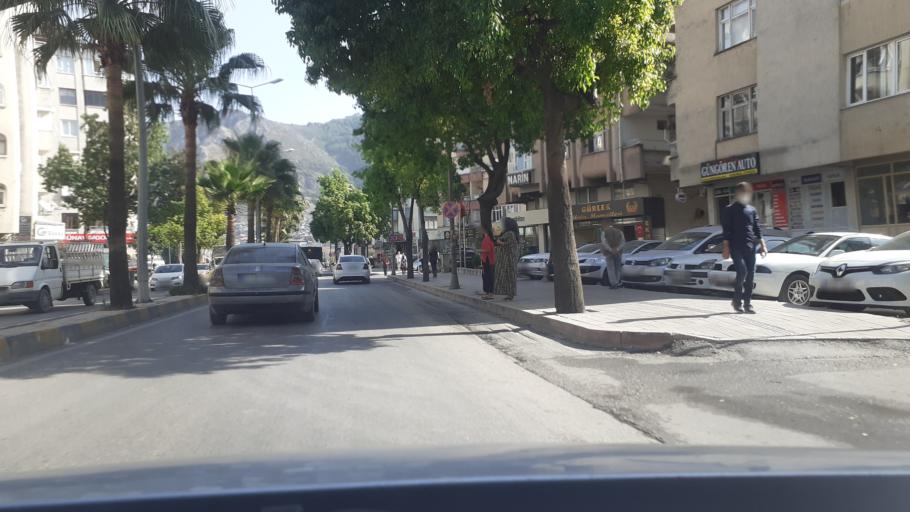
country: TR
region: Hatay
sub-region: Antakya Ilcesi
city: Antakya
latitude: 36.2106
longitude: 36.1602
